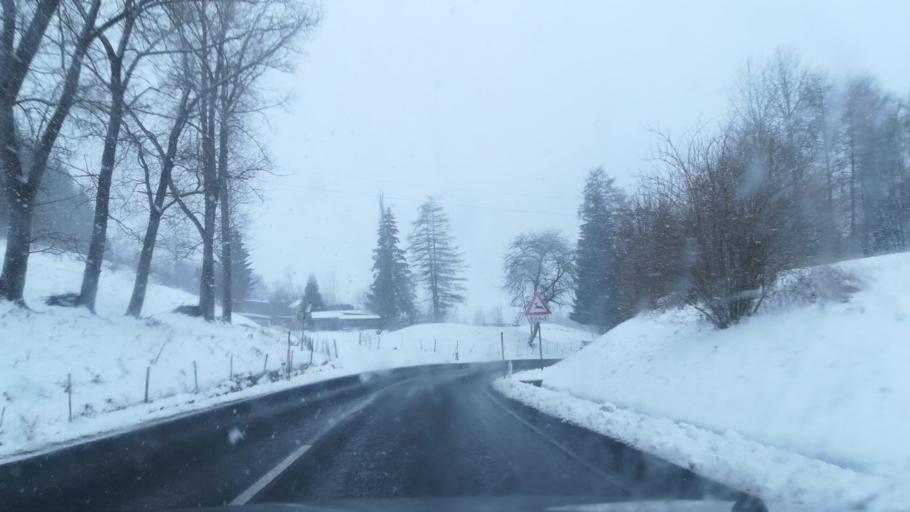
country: AT
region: Styria
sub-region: Politischer Bezirk Murtal
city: Poels
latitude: 47.2122
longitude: 14.5745
